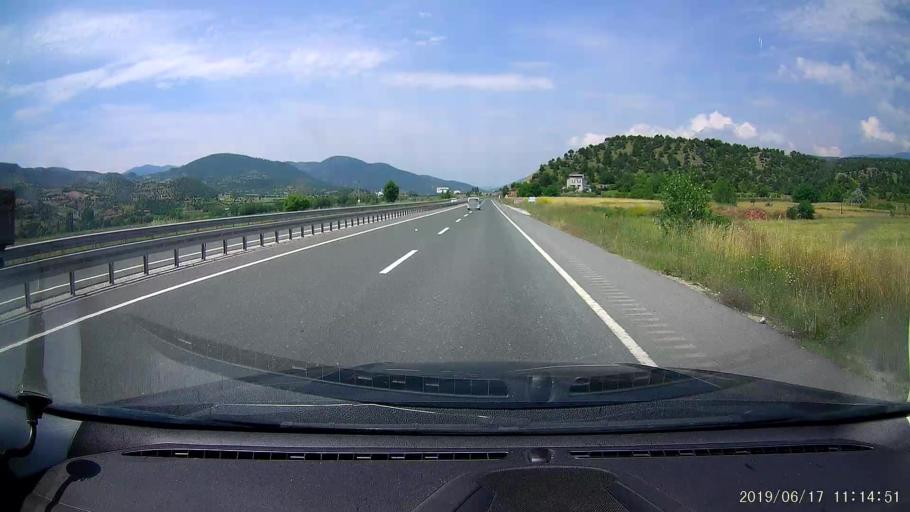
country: TR
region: Kastamonu
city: Tosya
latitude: 40.9552
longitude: 33.9368
